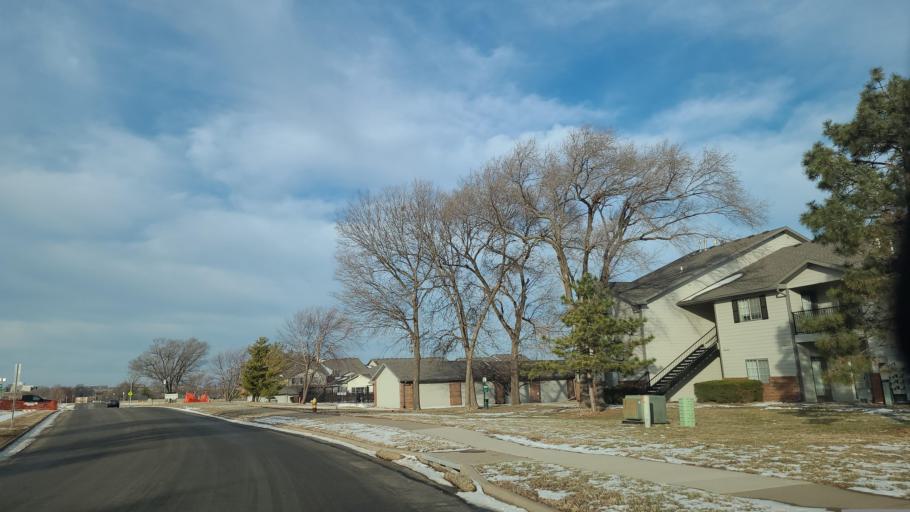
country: US
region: Kansas
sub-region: Douglas County
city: Lawrence
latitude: 38.9739
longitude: -95.2990
